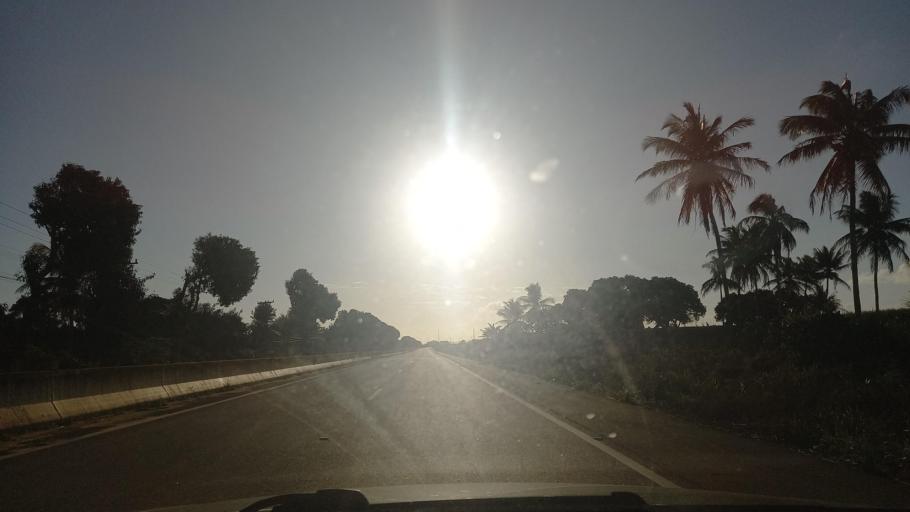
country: BR
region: Alagoas
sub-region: Campo Alegre
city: Campo Alegre
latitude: -9.7904
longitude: -36.3222
